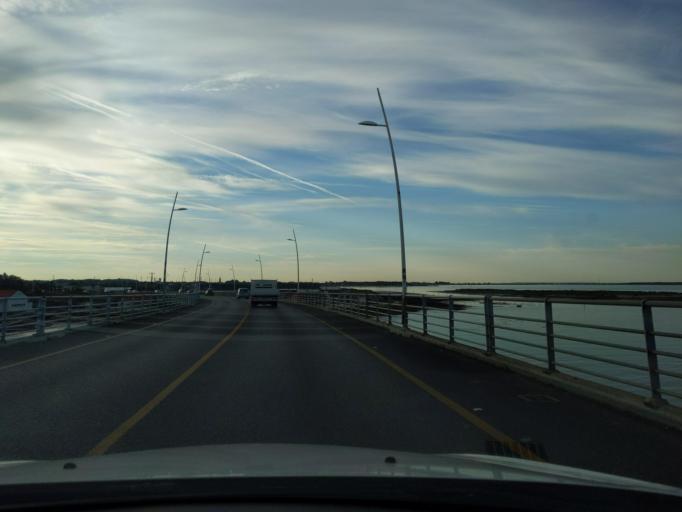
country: FR
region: Poitou-Charentes
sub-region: Departement de la Charente-Maritime
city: Bourcefranc-le-Chapus
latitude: 45.8430
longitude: -1.1776
